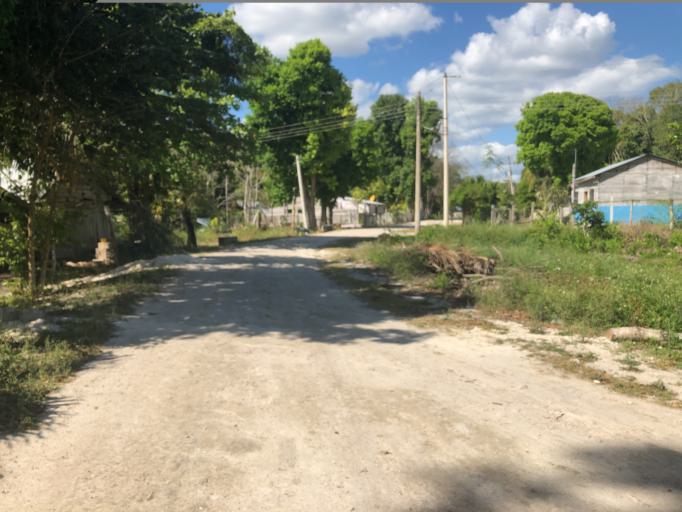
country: MX
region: Quintana Roo
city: Nicolas Bravo
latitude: 18.4504
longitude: -89.3065
